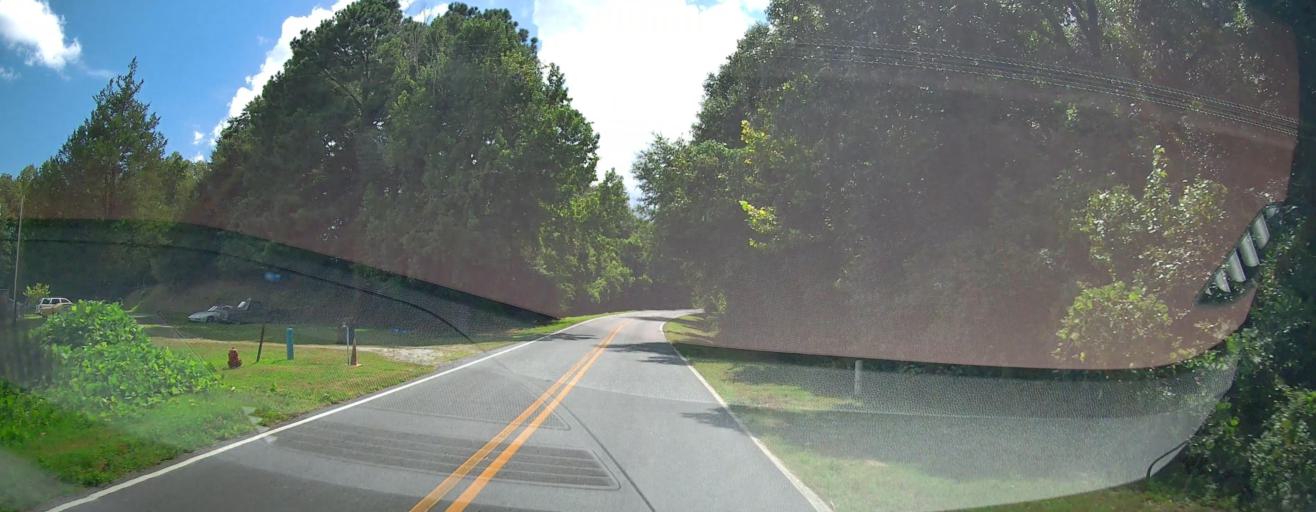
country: US
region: Georgia
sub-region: Chattahoochee County
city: Cusseta
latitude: 32.3056
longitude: -84.7697
